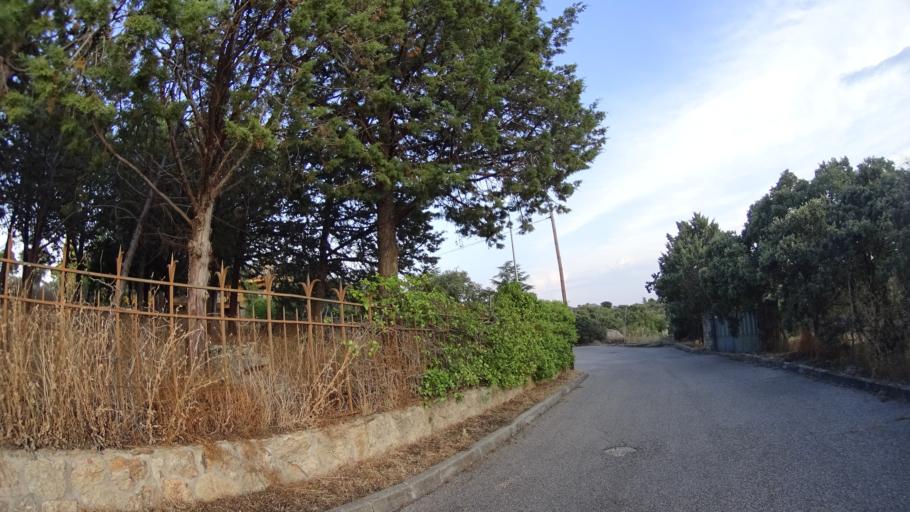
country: ES
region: Madrid
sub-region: Provincia de Madrid
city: Torrelodones
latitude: 40.5878
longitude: -3.9443
